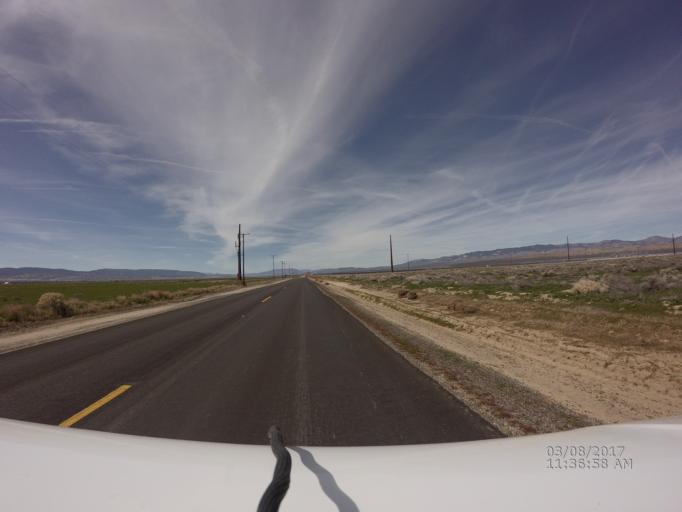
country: US
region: California
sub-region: Los Angeles County
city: Green Valley
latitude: 34.8188
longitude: -118.4295
